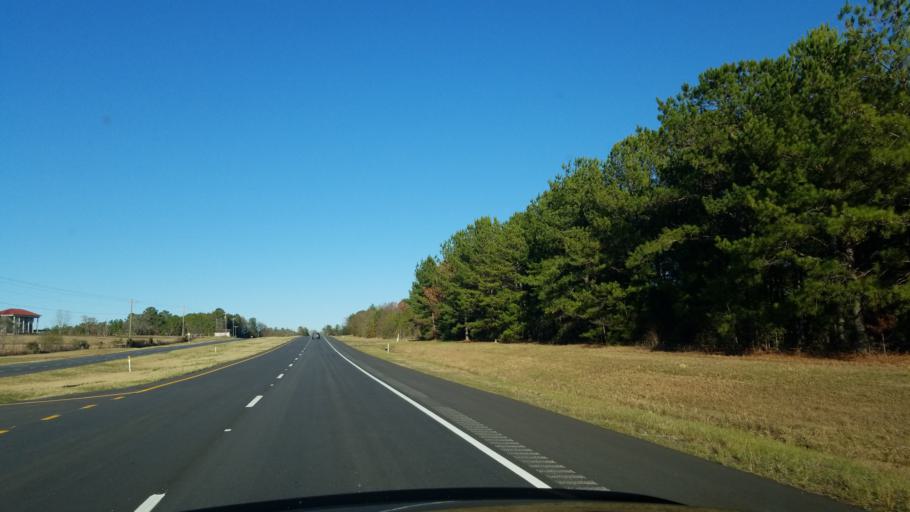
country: US
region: Georgia
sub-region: Talbot County
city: Talbotton
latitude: 32.5698
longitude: -84.6001
